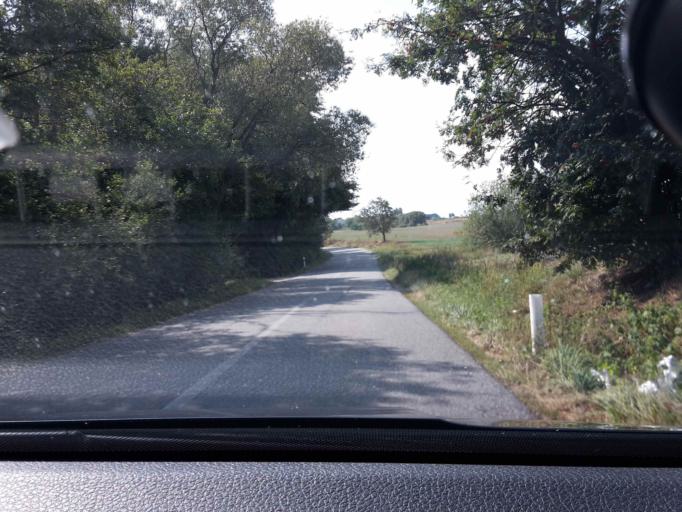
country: CZ
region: Vysocina
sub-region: Okres Jihlava
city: Trest'
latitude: 49.2707
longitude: 15.5751
